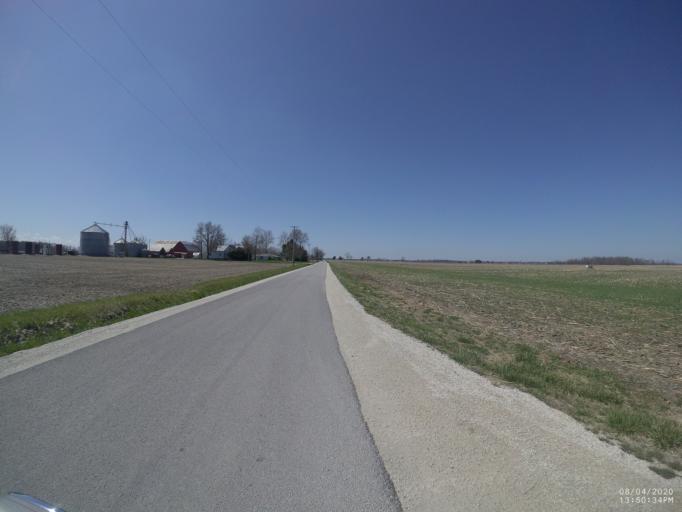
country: US
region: Ohio
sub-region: Sandusky County
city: Gibsonburg
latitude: 41.3265
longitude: -83.2919
